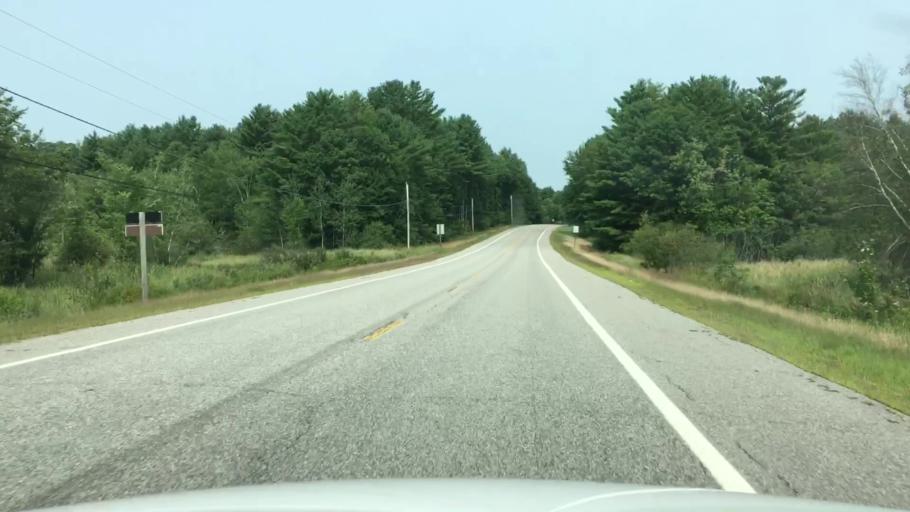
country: US
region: Maine
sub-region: Kennebec County
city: Wayne
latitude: 44.3594
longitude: -70.0837
